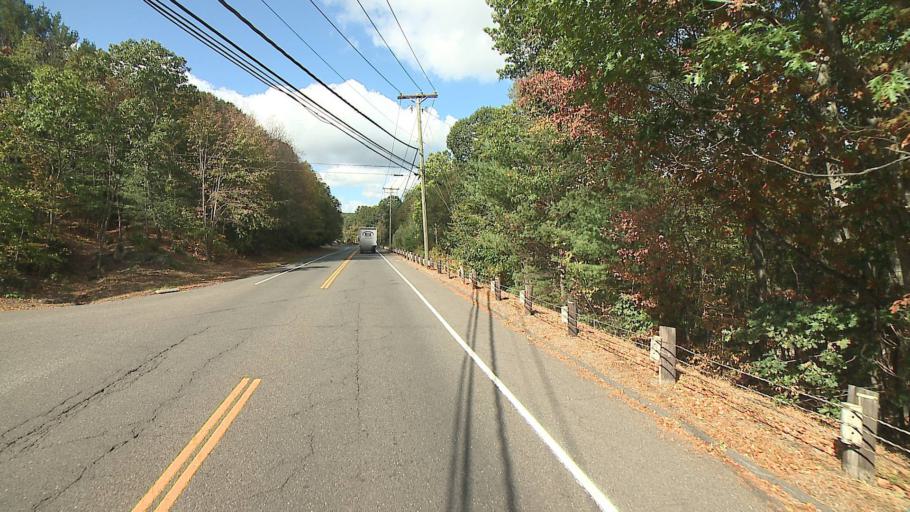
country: US
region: Connecticut
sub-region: New Haven County
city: Seymour
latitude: 41.4273
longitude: -73.0726
